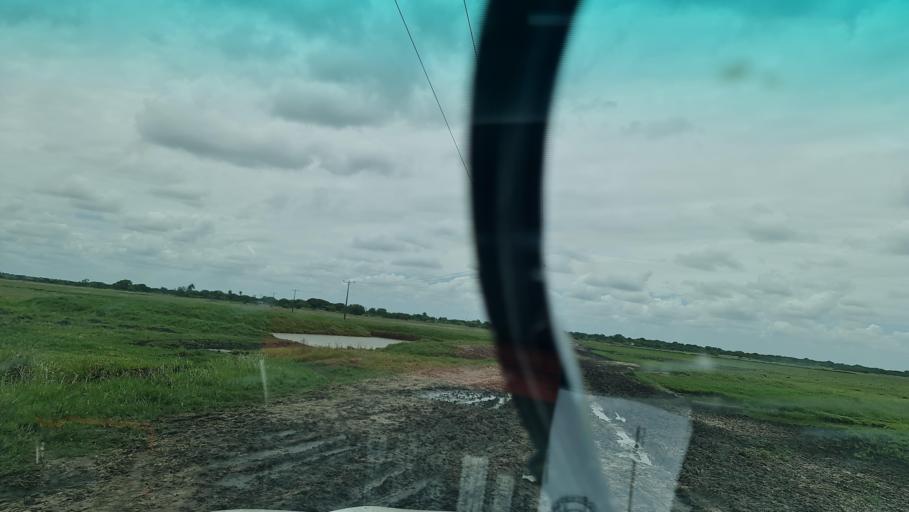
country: MZ
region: Maputo City
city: Maputo
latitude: -25.7078
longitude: 32.7033
